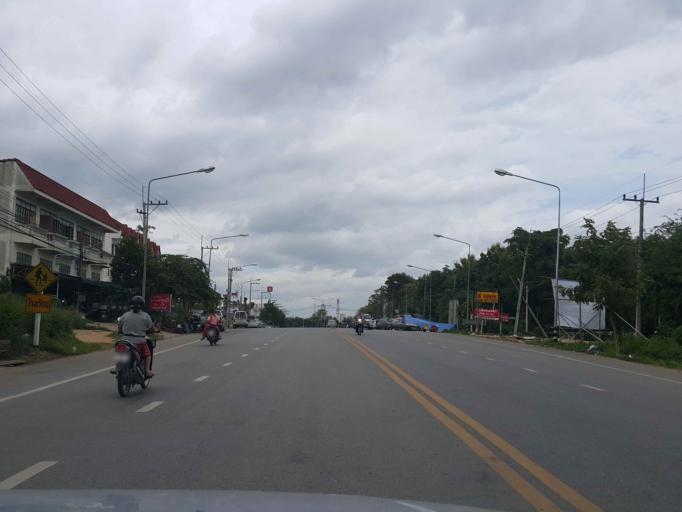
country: TH
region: Lamphun
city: Li
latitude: 17.7985
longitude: 98.9509
